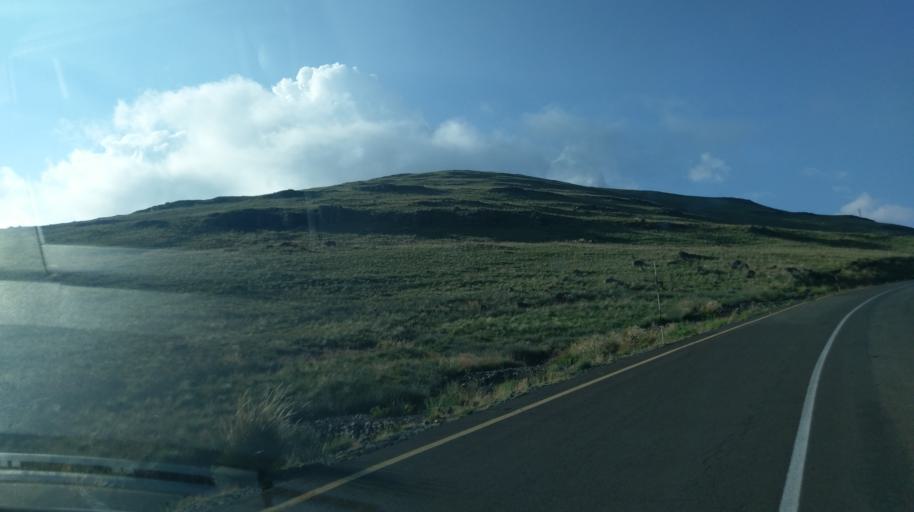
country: LS
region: Butha-Buthe
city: Butha-Buthe
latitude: -29.0797
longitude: 28.4253
